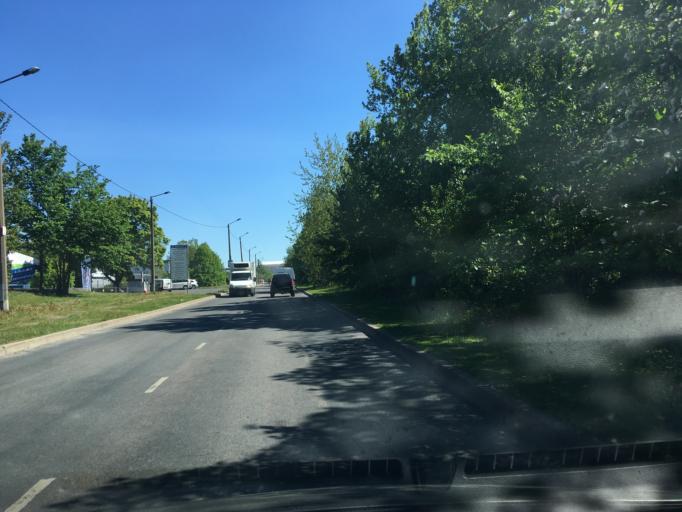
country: EE
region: Harju
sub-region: Saue vald
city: Laagri
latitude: 59.3977
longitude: 24.6495
